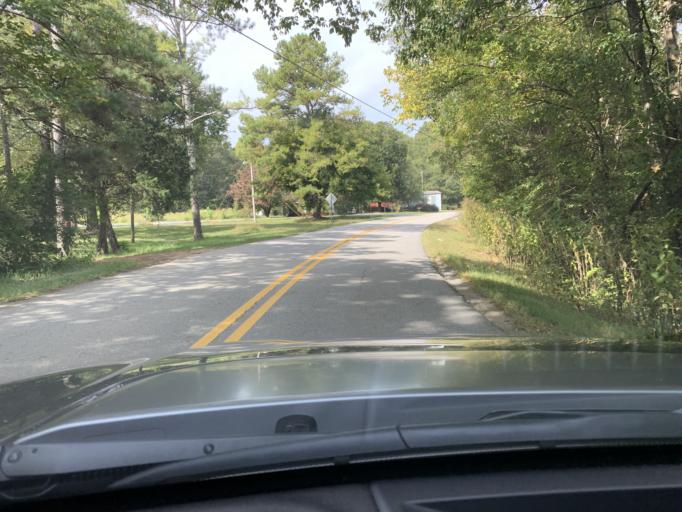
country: US
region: Georgia
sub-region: Polk County
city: Cedartown
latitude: 33.9710
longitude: -85.2681
